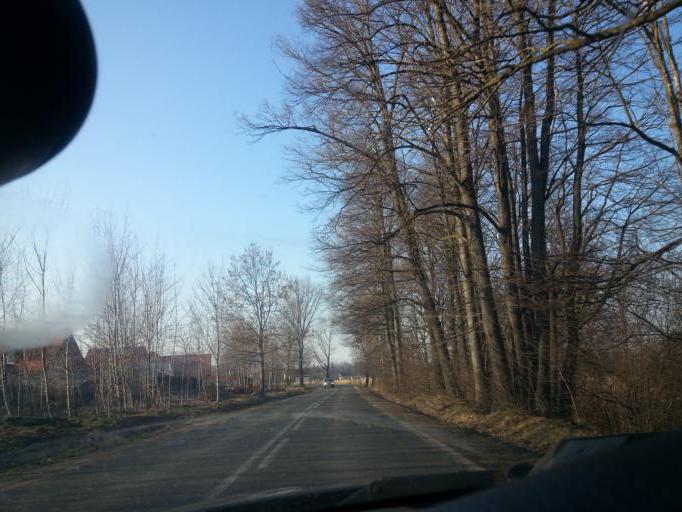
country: PL
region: Lower Silesian Voivodeship
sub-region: Powiat jeleniogorski
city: Myslakowice
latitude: 50.8301
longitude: 15.7925
